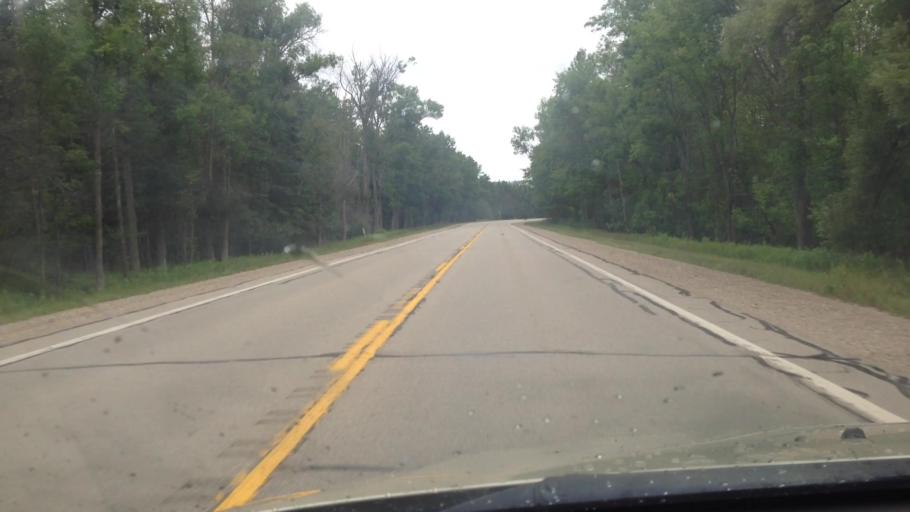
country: US
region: Michigan
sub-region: Menominee County
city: Menominee
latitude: 45.4234
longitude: -87.3492
